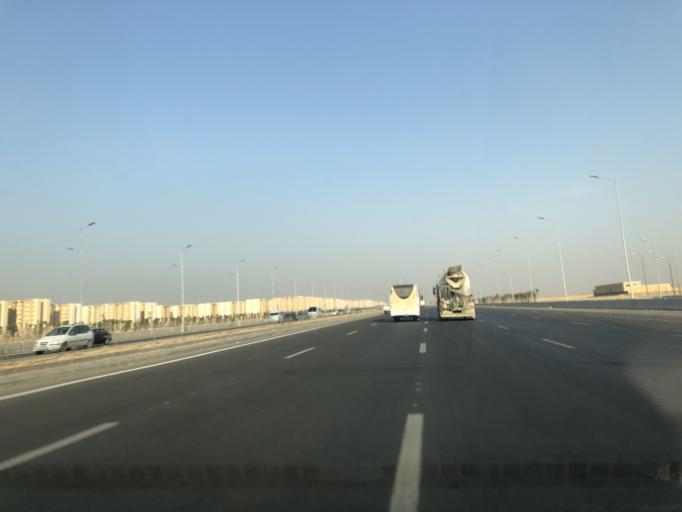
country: EG
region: Al Jizah
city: Madinat Sittah Uktubar
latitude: 29.9060
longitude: 30.9484
